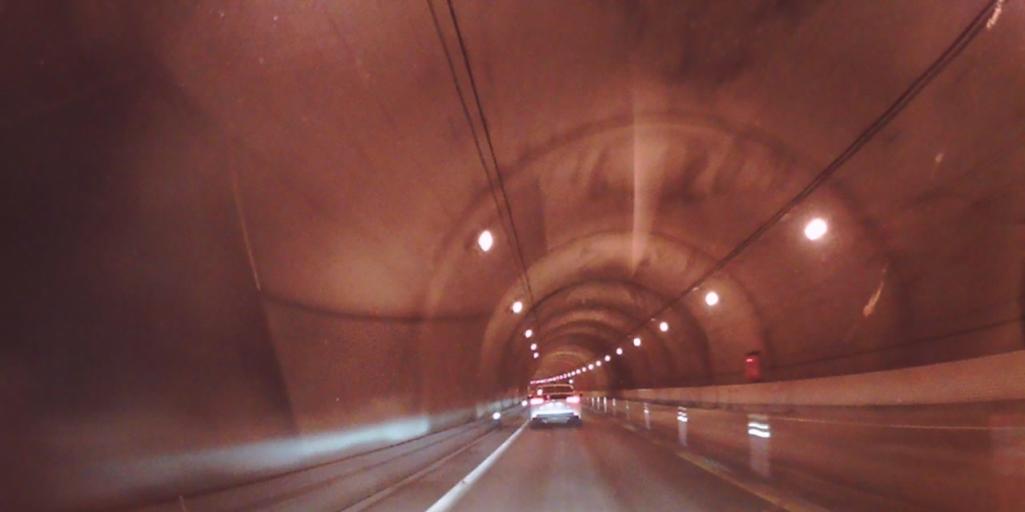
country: JP
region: Hokkaido
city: Date
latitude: 42.5544
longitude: 140.7843
